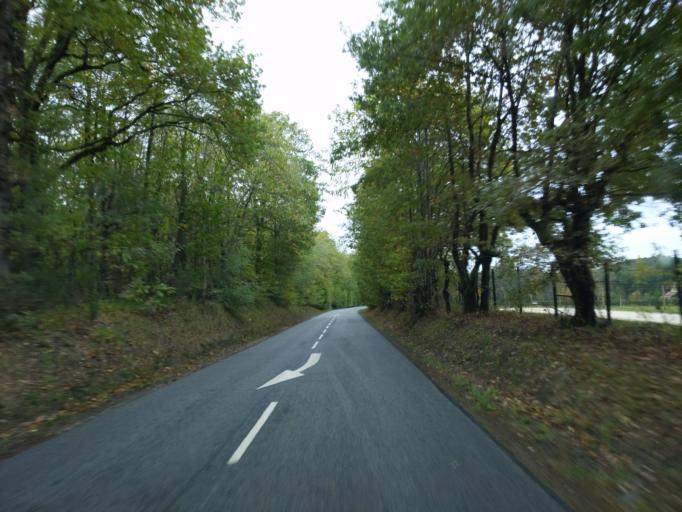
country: FR
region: Ile-de-France
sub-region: Departement des Yvelines
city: Bullion
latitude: 48.6100
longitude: 1.9974
